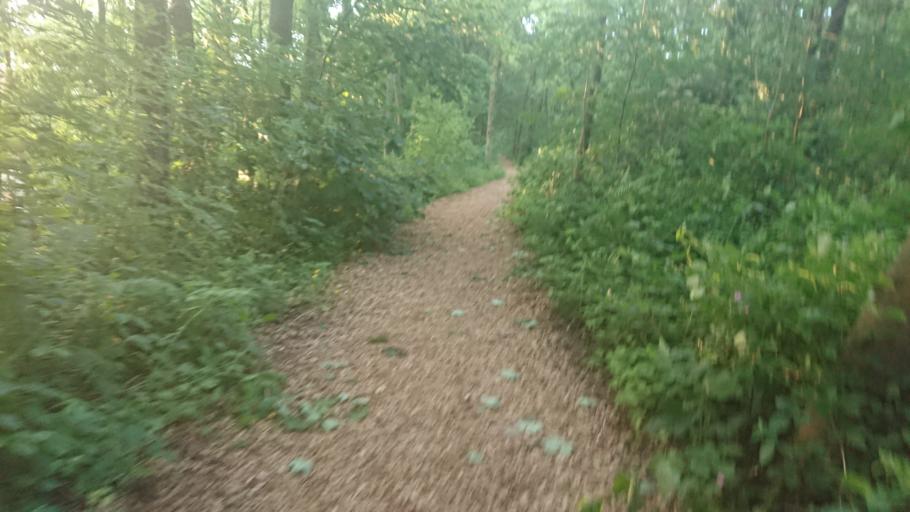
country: GB
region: England
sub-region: Lancashire
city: Galgate
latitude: 54.0055
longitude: -2.7828
